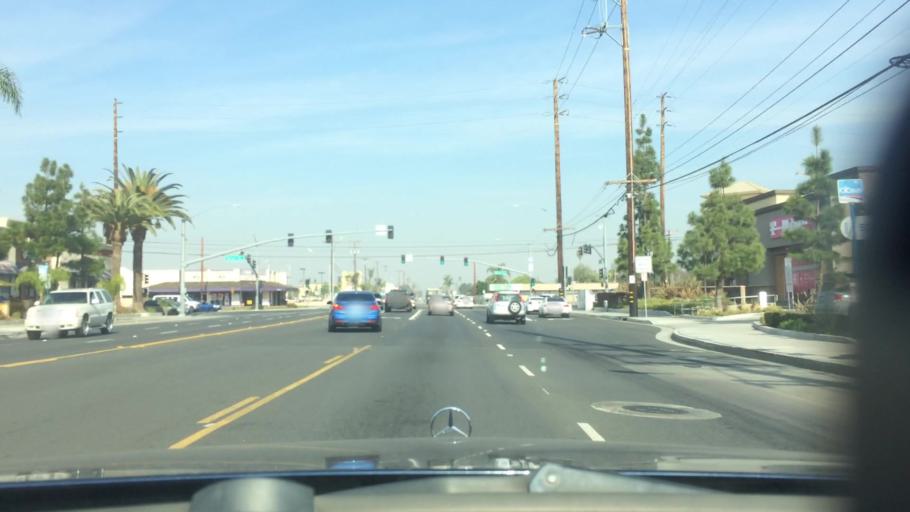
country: US
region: California
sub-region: Orange County
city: Santa Ana
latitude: 33.7152
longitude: -117.8853
